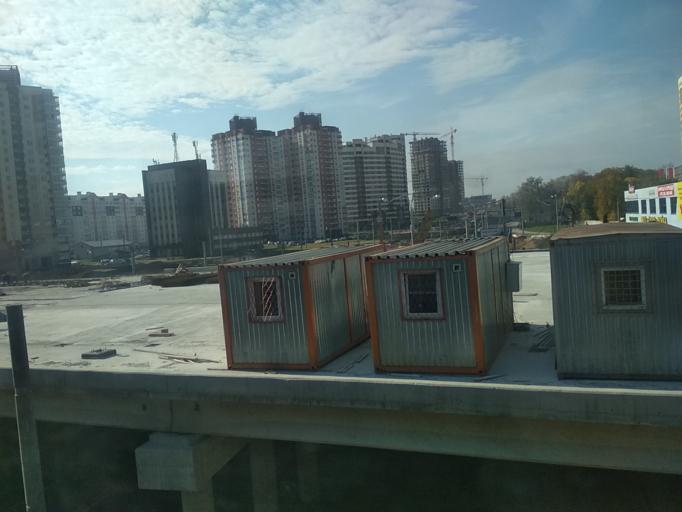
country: BY
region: Minsk
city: Minsk
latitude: 53.8724
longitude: 27.5619
